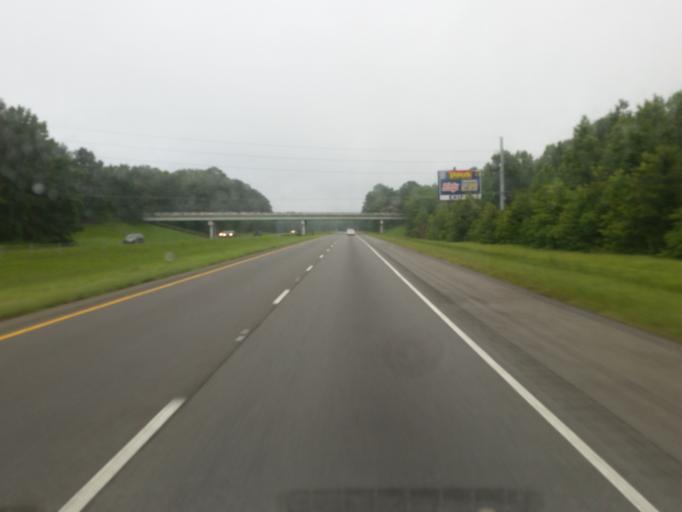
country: US
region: Louisiana
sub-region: Bossier Parish
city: Eastwood
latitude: 32.5417
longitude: -93.5401
